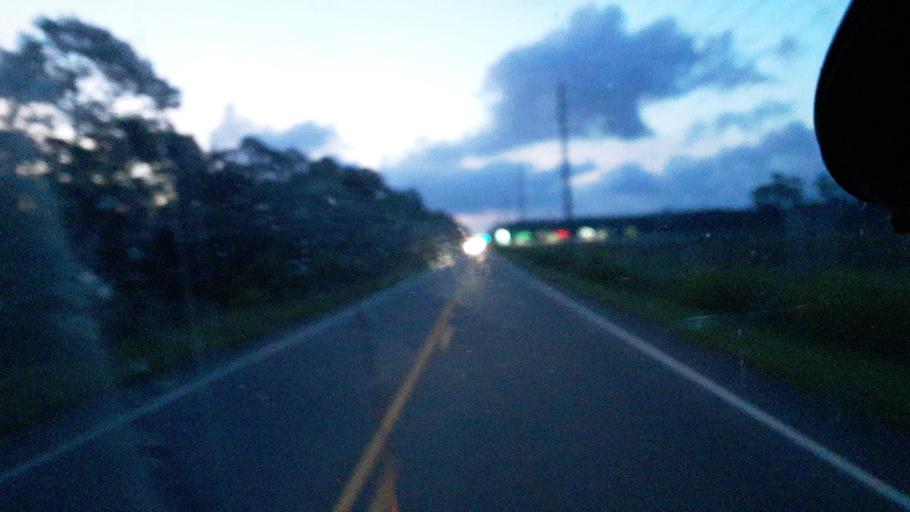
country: US
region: North Carolina
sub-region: Brunswick County
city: Oak Island
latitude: 33.9878
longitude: -78.1957
